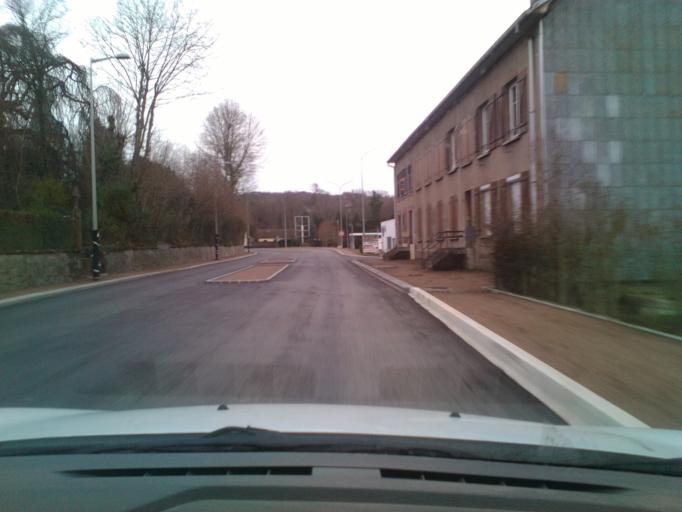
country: FR
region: Lorraine
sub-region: Departement des Vosges
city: Moyenmoutier
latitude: 48.3772
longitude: 6.9045
